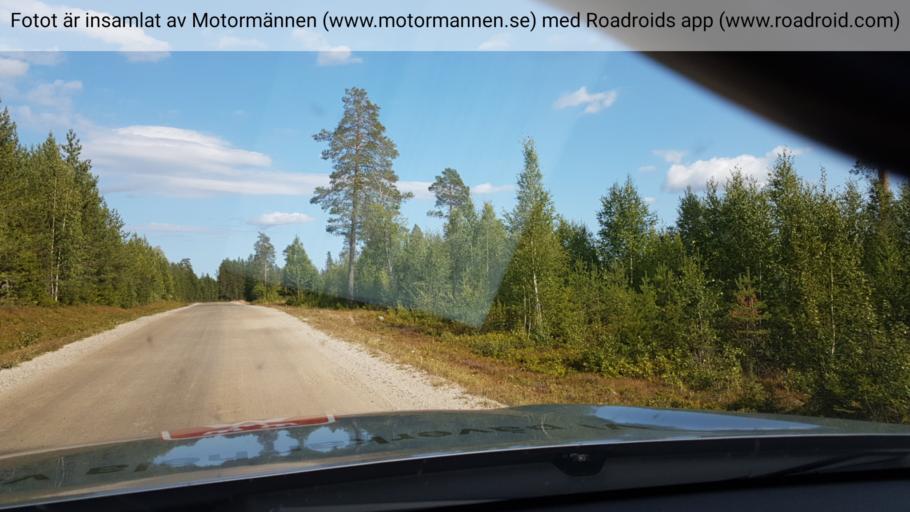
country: SE
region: Vaesterbotten
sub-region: Skelleftea Kommun
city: Backa
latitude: 65.2003
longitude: 20.9907
